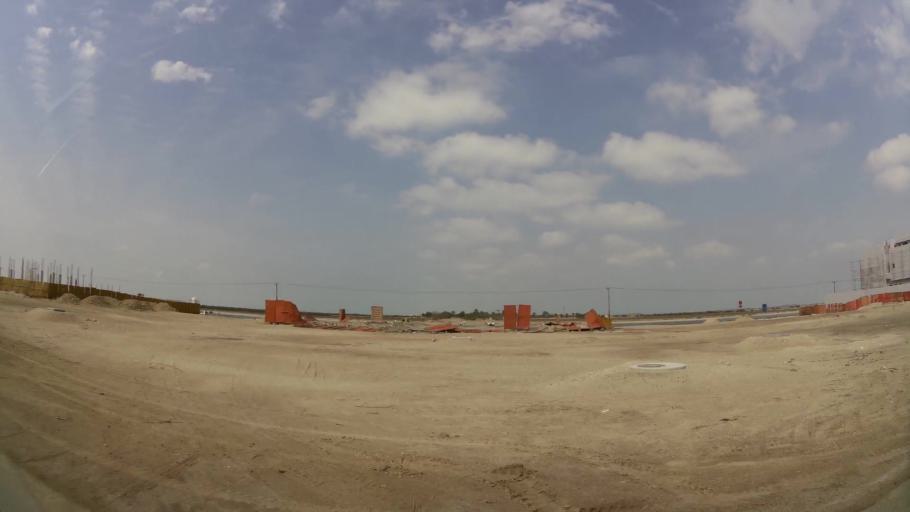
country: AE
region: Abu Dhabi
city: Abu Dhabi
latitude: 24.5774
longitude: 54.6437
